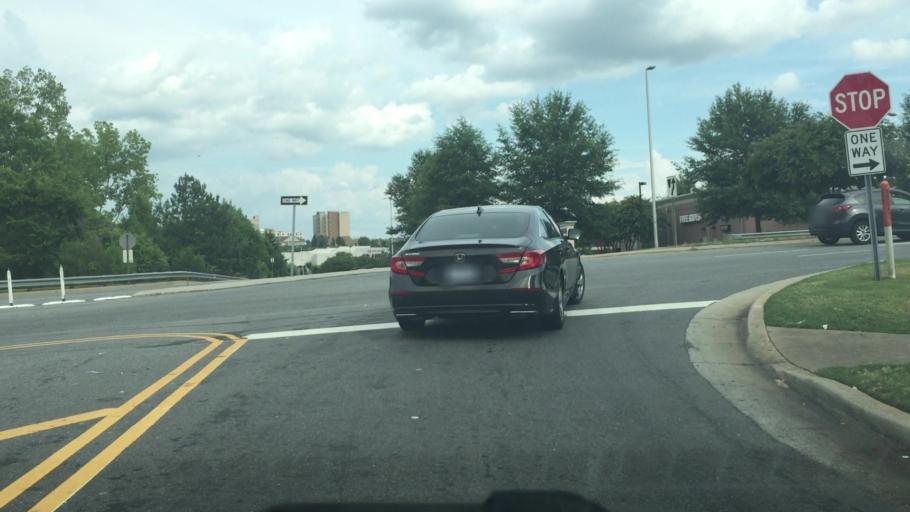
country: US
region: North Carolina
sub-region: Cabarrus County
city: Harrisburg
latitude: 35.3673
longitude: -80.7098
